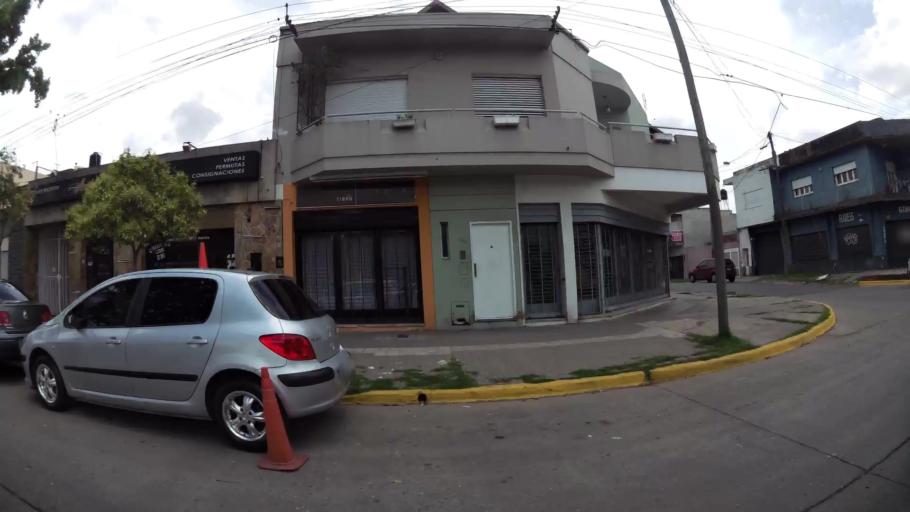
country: AR
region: Santa Fe
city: Gobernador Galvez
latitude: -32.9911
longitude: -60.6551
